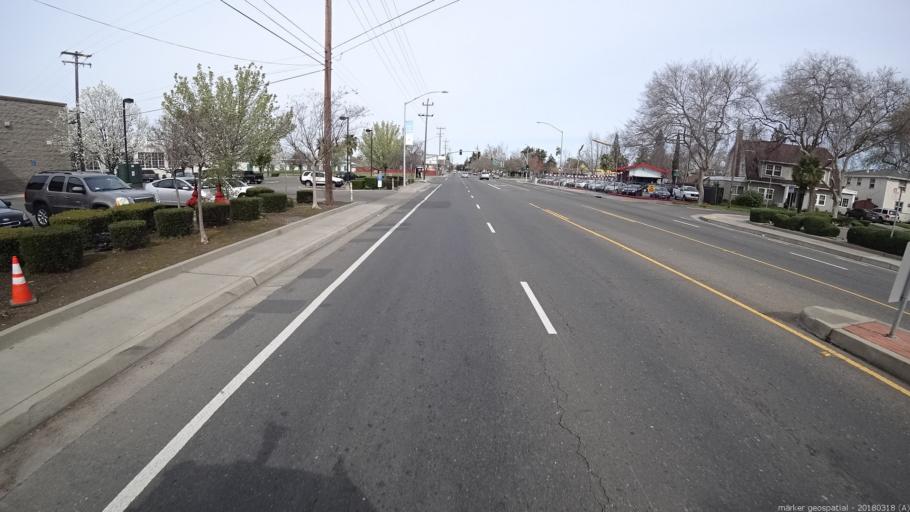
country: US
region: California
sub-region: Sacramento County
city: Parkway
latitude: 38.5309
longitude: -121.4454
